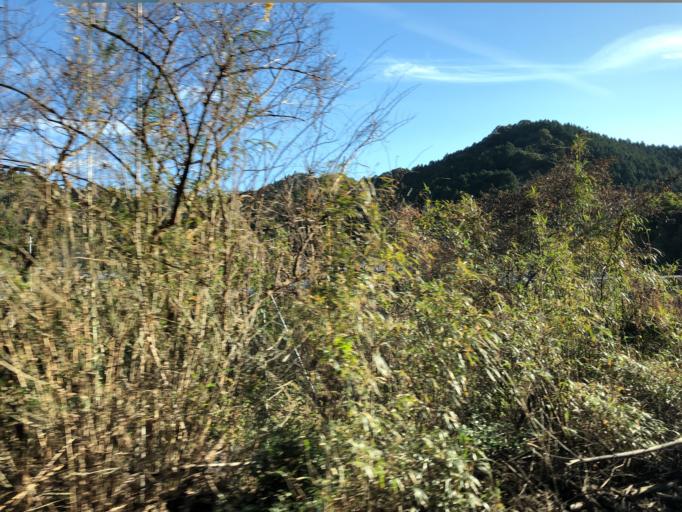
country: JP
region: Kochi
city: Nakamura
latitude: 33.1224
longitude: 133.1190
